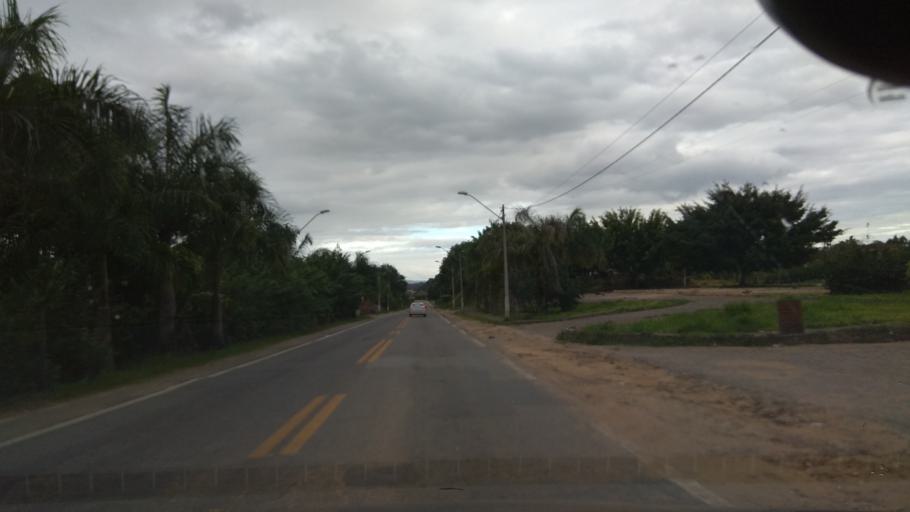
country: BR
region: Bahia
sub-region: Ubata
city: Ubata
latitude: -14.2039
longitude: -39.5313
